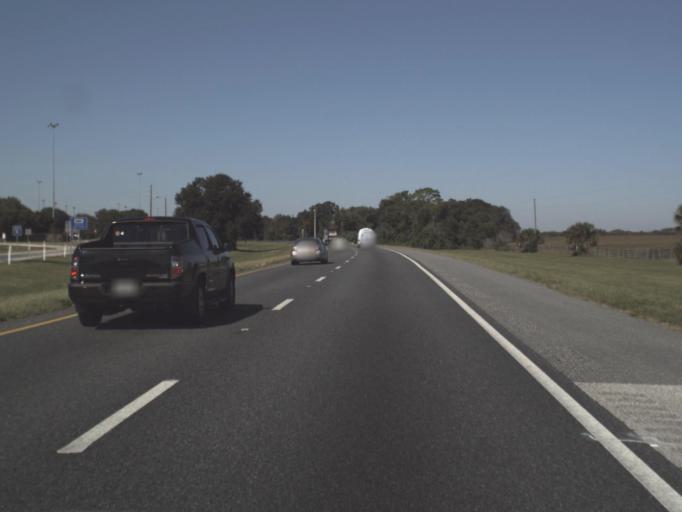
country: US
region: Florida
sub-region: Sumter County
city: Wildwood
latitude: 28.7857
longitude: -81.9785
